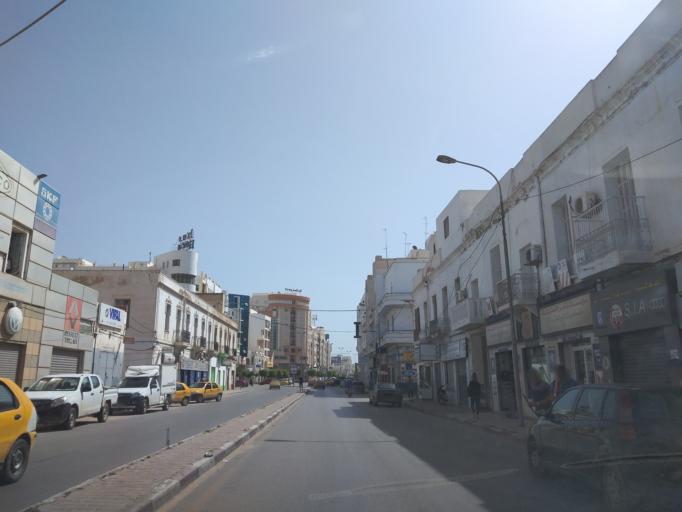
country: TN
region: Safaqis
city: Sfax
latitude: 34.7351
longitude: 10.7531
